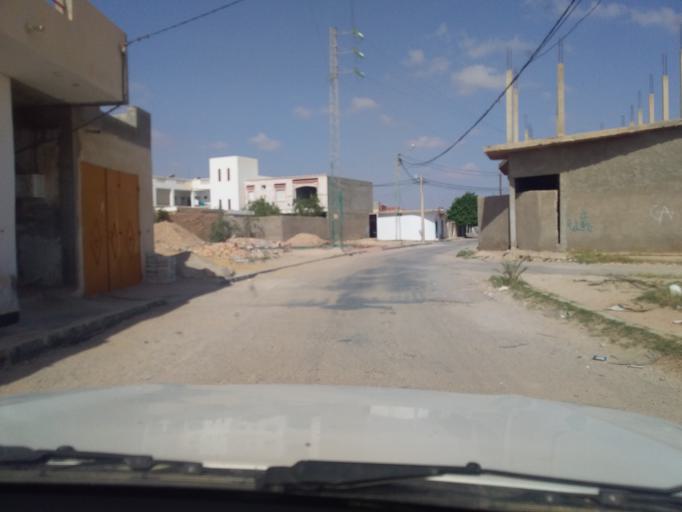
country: TN
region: Madanin
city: Medenine
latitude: 33.5835
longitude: 10.3235
